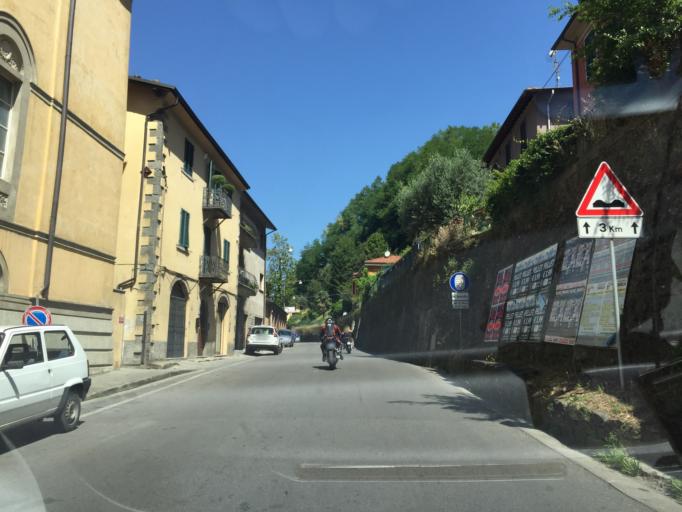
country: IT
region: Tuscany
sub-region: Provincia di Lucca
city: Castelnuovo di Garfagnana
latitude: 44.1126
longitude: 10.4126
